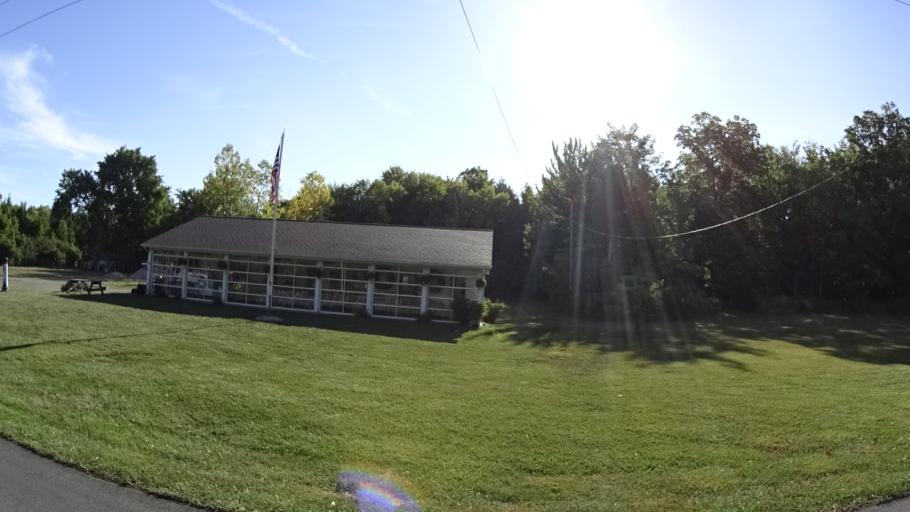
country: US
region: Ohio
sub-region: Erie County
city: Sandusky
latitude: 41.6077
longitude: -82.7083
